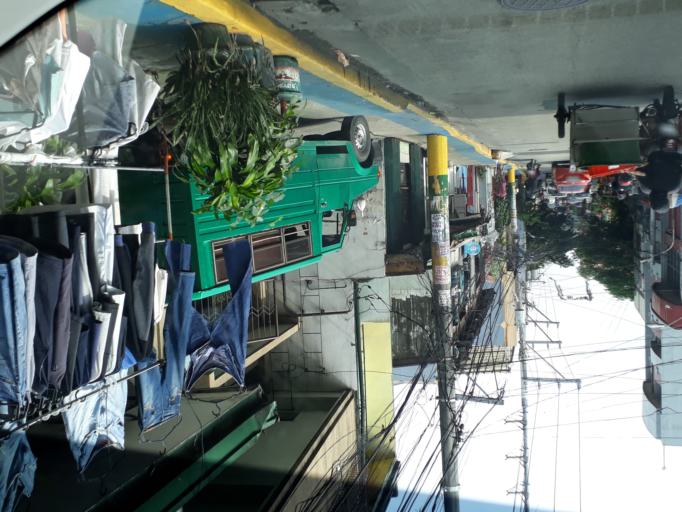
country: PH
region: Metro Manila
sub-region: City of Manila
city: Manila
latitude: 14.6329
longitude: 120.9795
